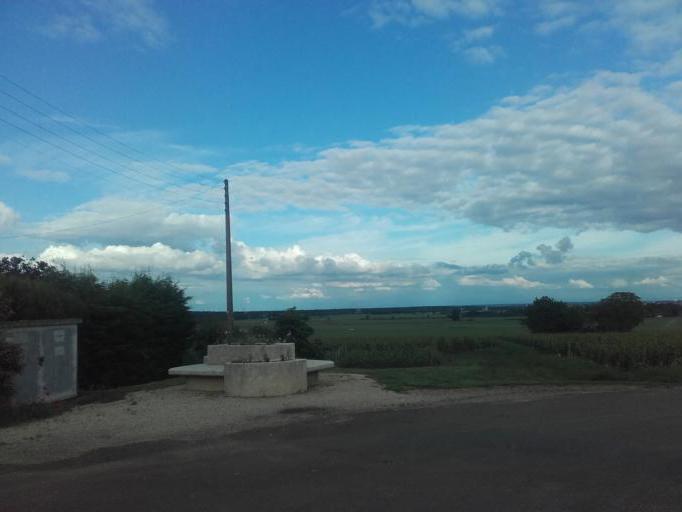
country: FR
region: Bourgogne
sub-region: Departement de Saone-et-Loire
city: Rully
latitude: 46.8715
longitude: 4.7464
